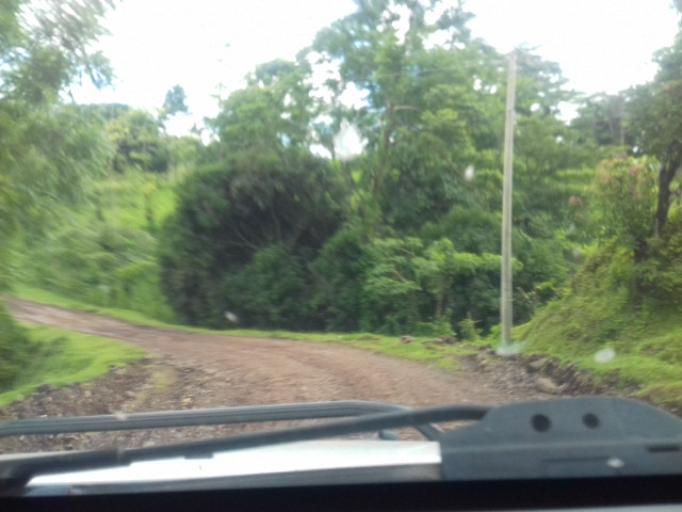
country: NI
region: Matagalpa
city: Rio Blanco
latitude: 12.9926
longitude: -85.1913
